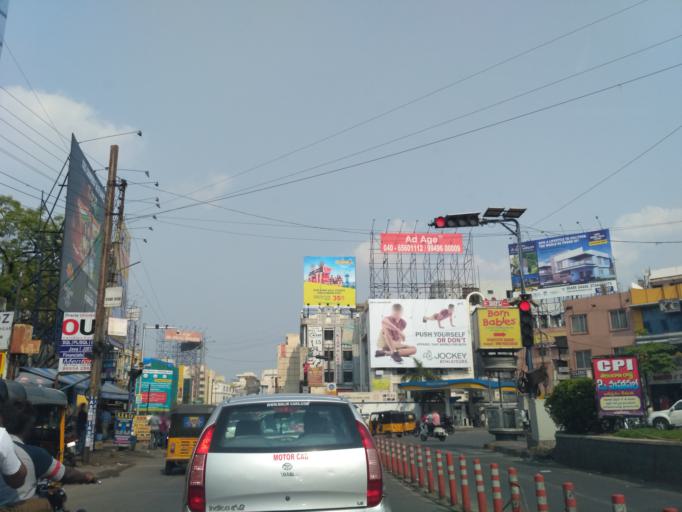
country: IN
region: Telangana
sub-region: Hyderabad
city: Hyderabad
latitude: 17.4008
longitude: 78.4877
